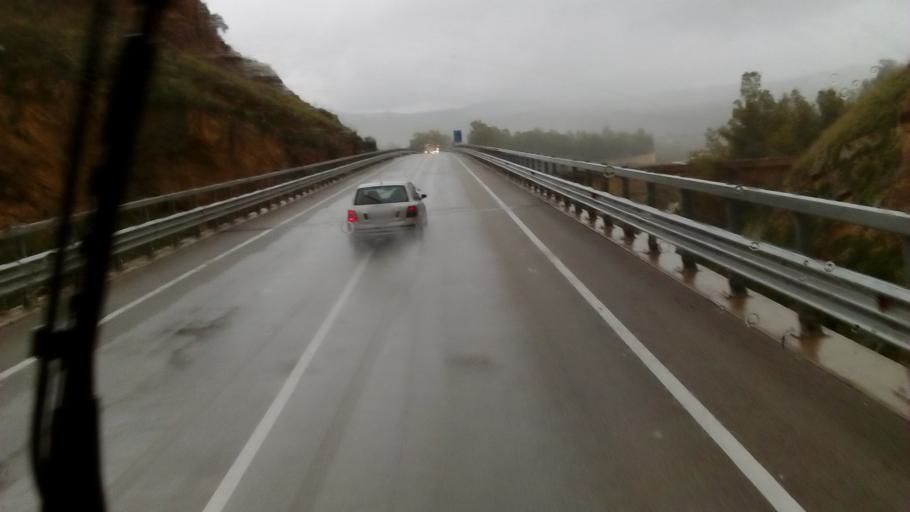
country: IT
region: Sicily
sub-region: Enna
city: Pietraperzia
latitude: 37.4972
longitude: 14.1438
